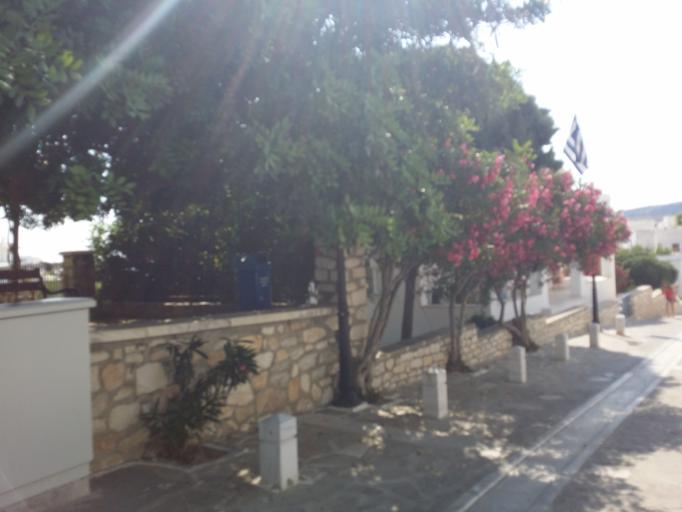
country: GR
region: South Aegean
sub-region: Nomos Kykladon
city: Paros
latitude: 37.0563
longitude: 25.2067
